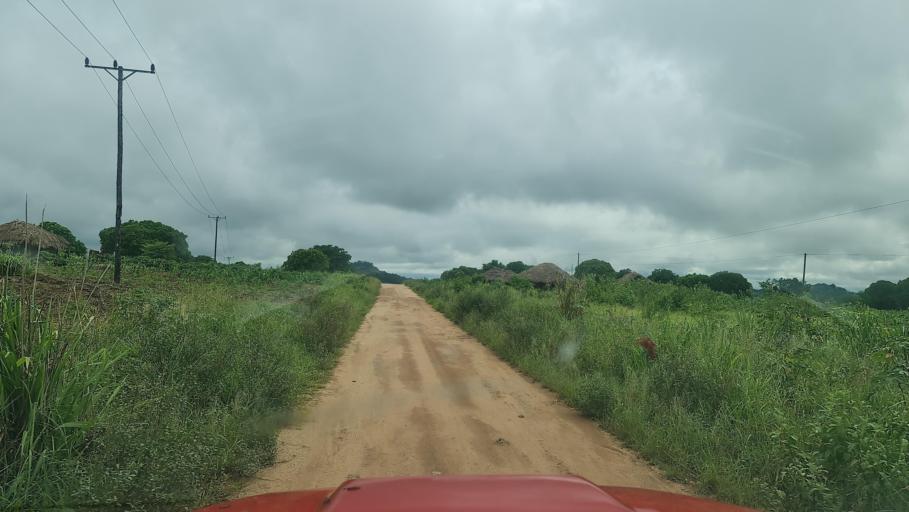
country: MW
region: Southern Region
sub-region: Nsanje District
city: Nsanje
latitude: -17.1838
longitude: 35.9269
